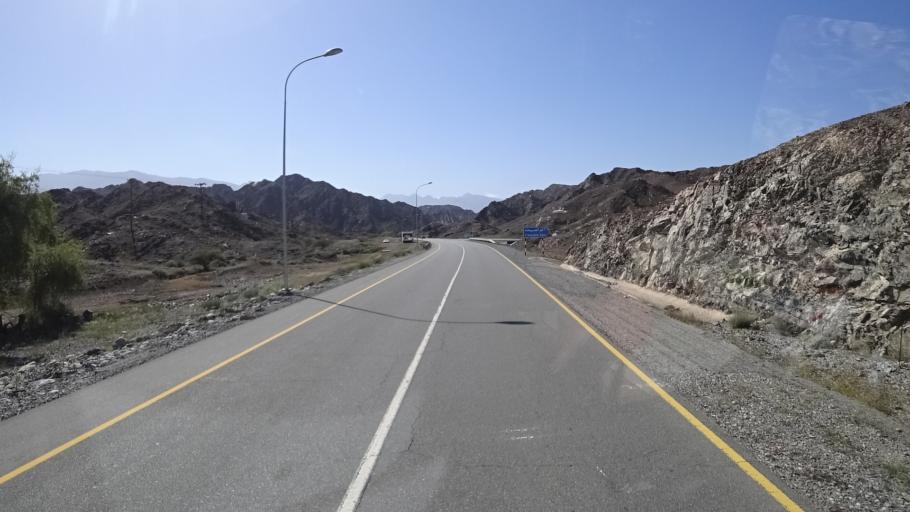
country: OM
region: Al Batinah
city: Bayt al `Awabi
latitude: 23.3647
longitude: 57.6719
